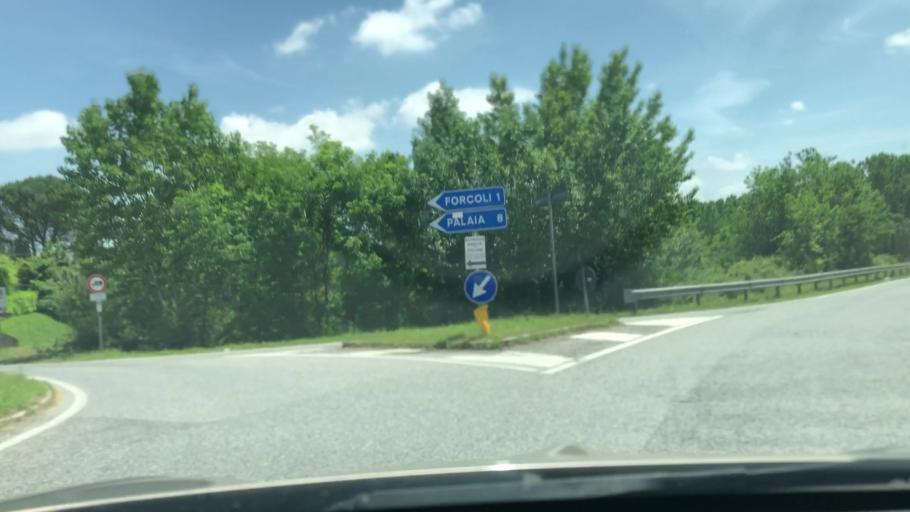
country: IT
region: Tuscany
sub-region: Province of Pisa
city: Forcoli
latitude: 43.6094
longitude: 10.6900
